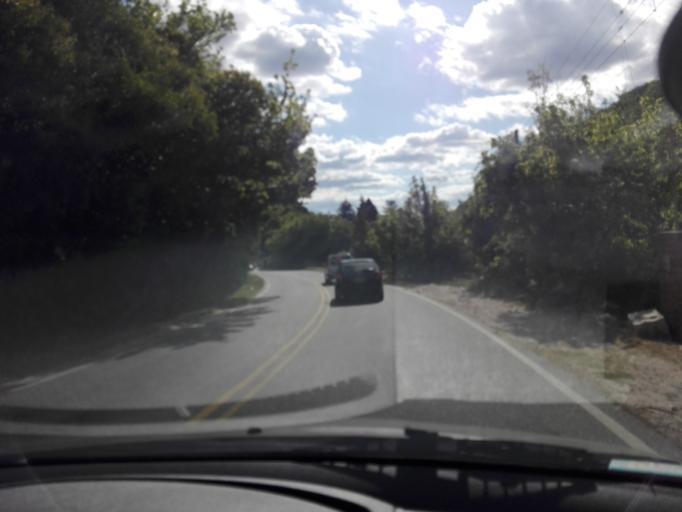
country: AR
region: Cordoba
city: Villa Las Rosas
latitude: -31.9088
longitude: -64.9990
